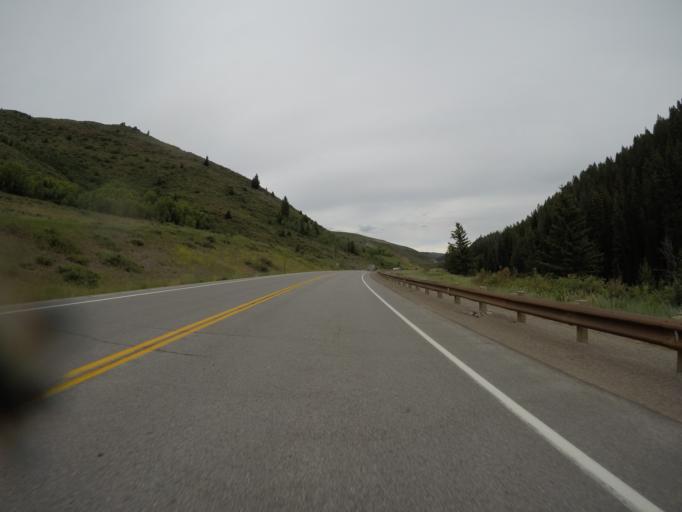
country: US
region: Wyoming
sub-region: Lincoln County
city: Afton
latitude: 42.4887
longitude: -110.9493
